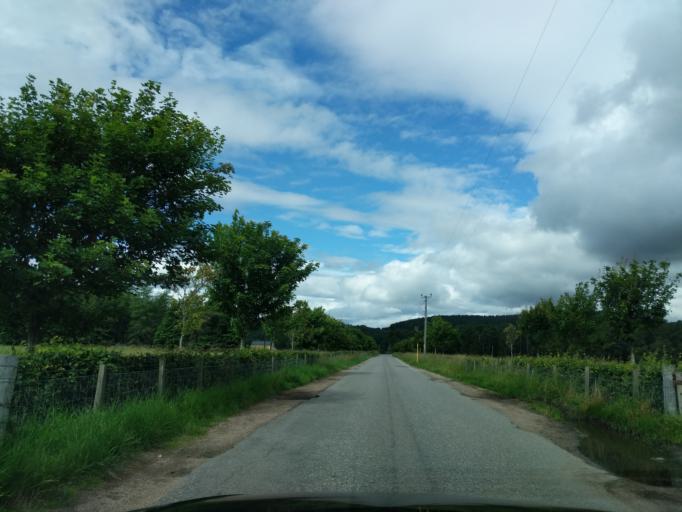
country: GB
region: Scotland
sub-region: Aberdeenshire
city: Ballater
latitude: 57.0405
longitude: -3.0492
